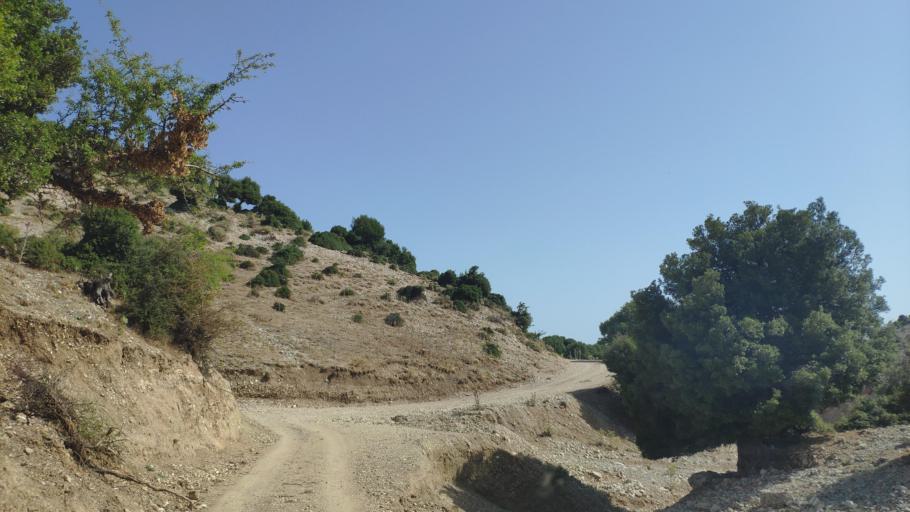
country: GR
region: West Greece
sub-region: Nomos Aitolias kai Akarnanias
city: Monastirakion
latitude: 38.8041
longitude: 20.9971
